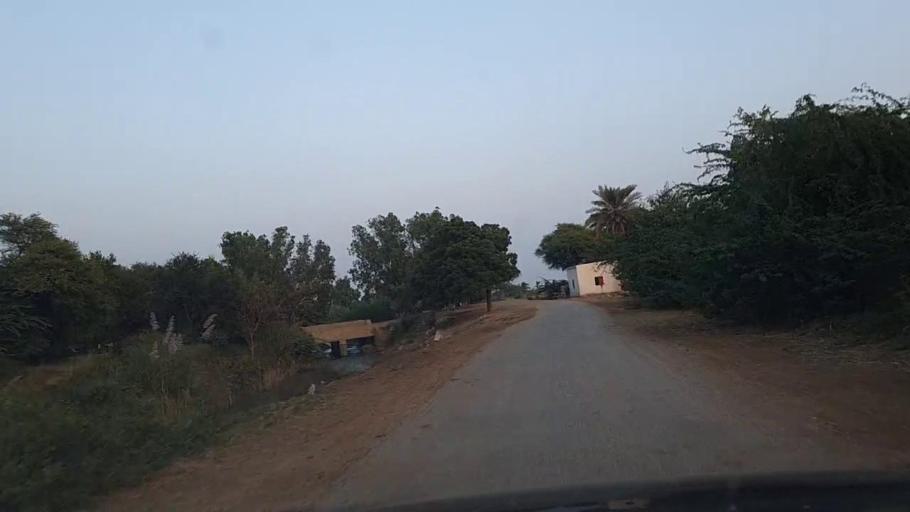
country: PK
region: Sindh
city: Mirpur Sakro
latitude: 24.6279
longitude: 67.6507
